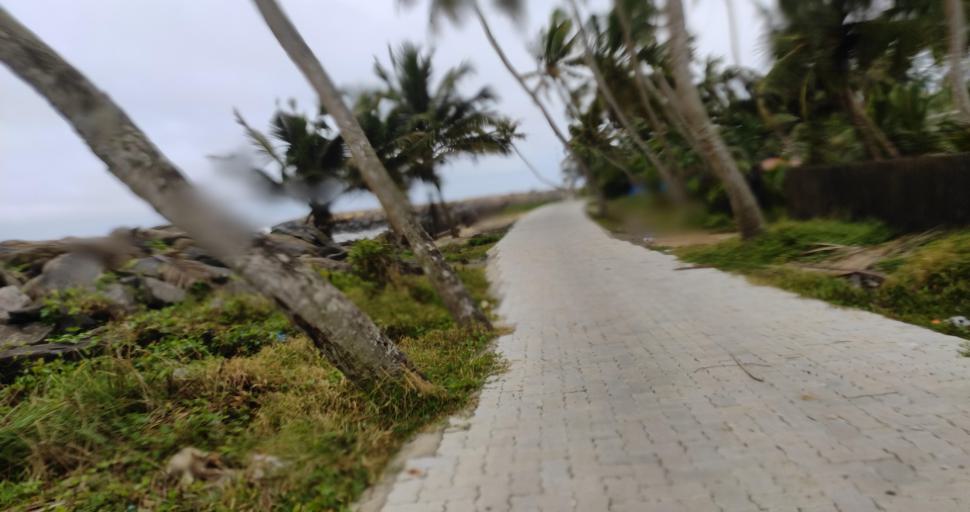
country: IN
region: Kerala
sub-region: Alappuzha
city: Vayalar
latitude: 9.6774
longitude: 76.2911
